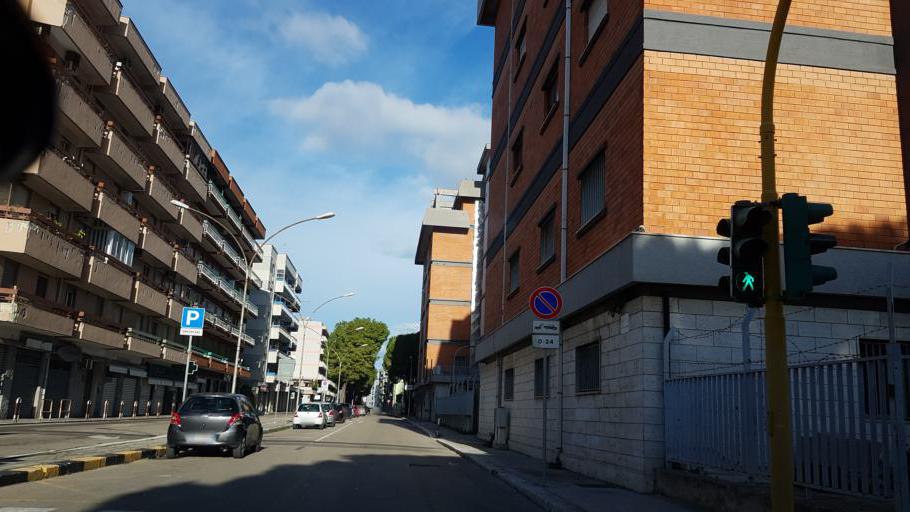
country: IT
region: Apulia
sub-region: Provincia di Brindisi
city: Brindisi
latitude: 40.6260
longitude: 17.9283
